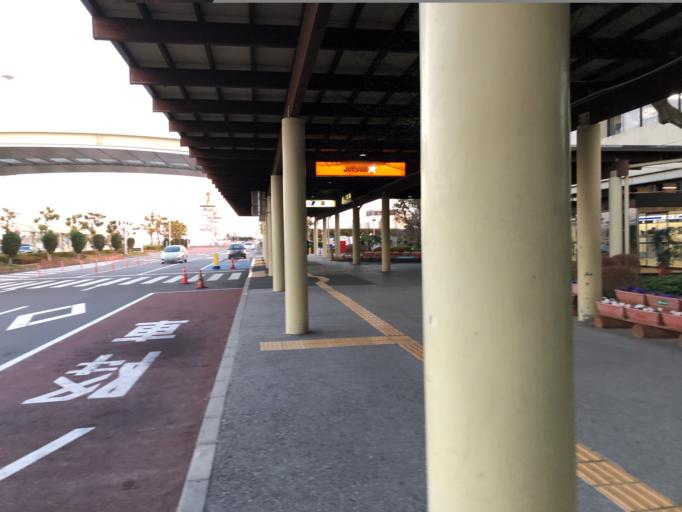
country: JP
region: Kochi
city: Kochi-shi
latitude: 33.5477
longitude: 133.6746
